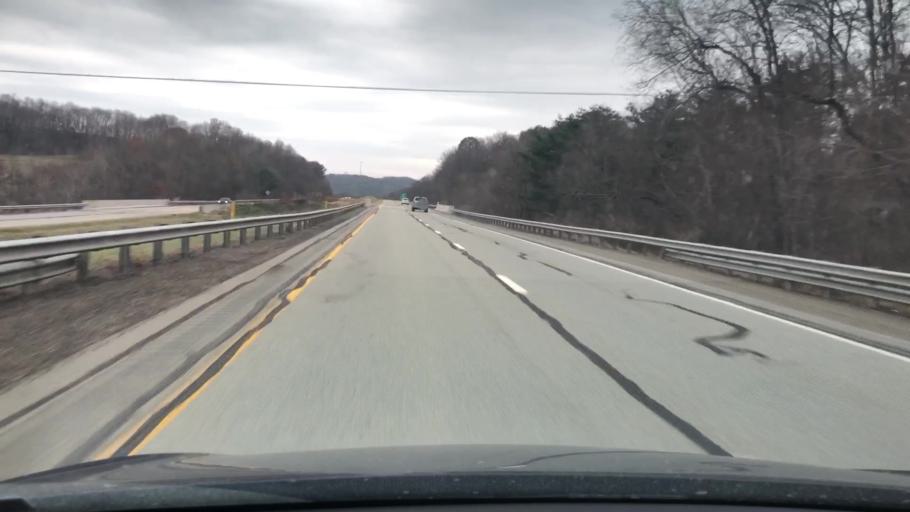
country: US
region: Pennsylvania
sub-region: Armstrong County
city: Ford City
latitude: 40.7780
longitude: -79.5961
